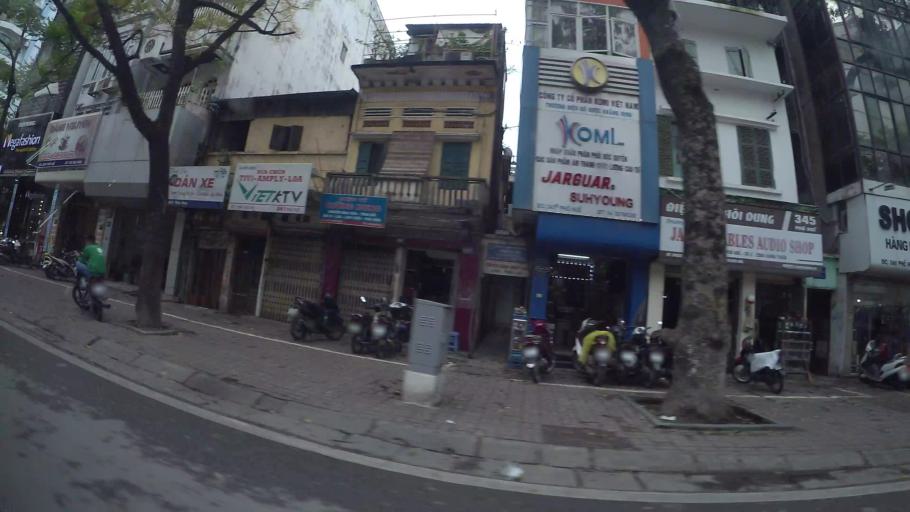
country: VN
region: Ha Noi
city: Hai BaTrung
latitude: 21.0096
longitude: 105.8517
